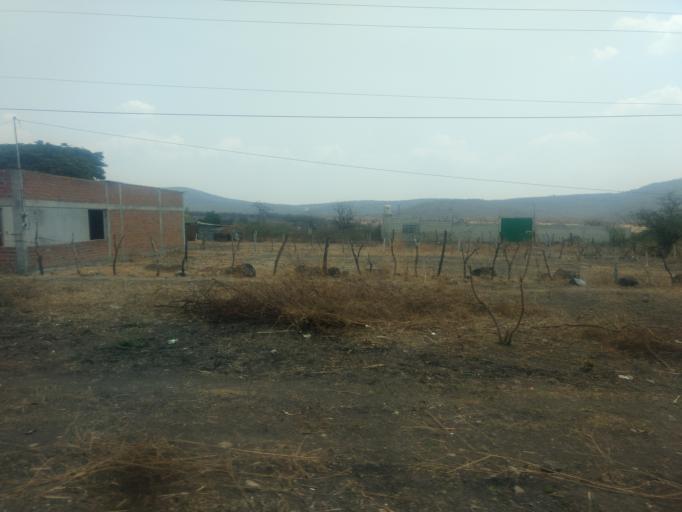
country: MX
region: Morelos
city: La Joya
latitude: 18.6691
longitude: -99.4280
